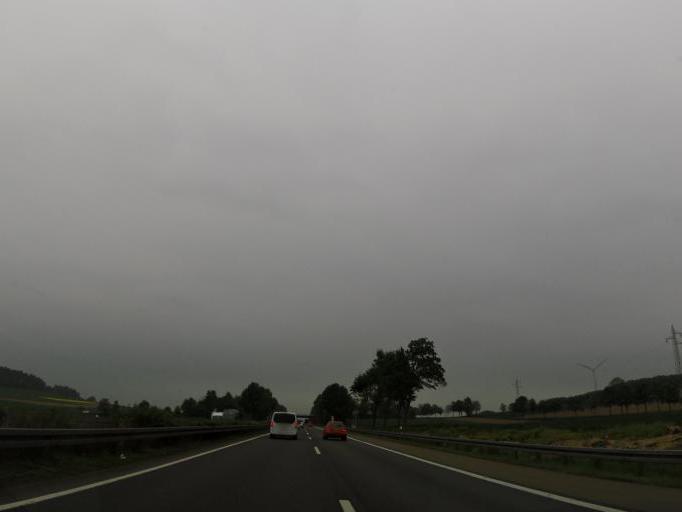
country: DE
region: Lower Saxony
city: Gittelde
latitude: 51.8310
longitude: 10.1147
